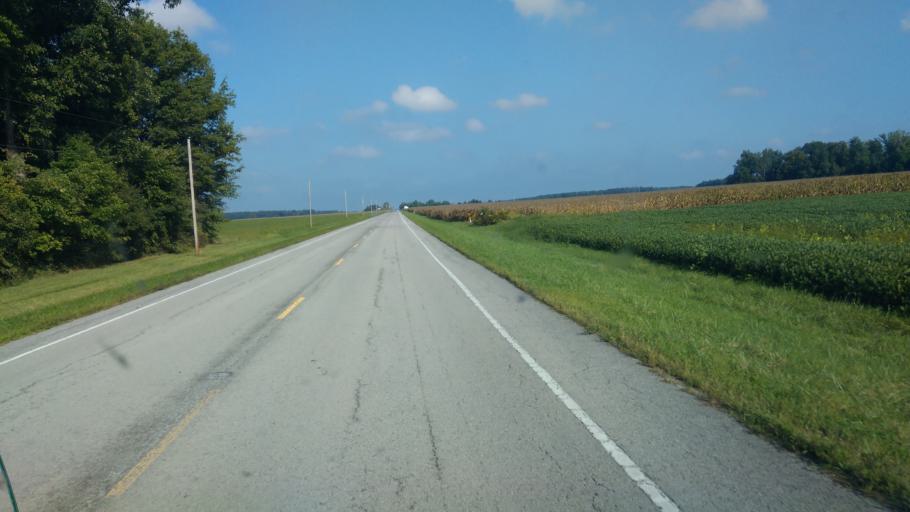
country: US
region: Ohio
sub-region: Hancock County
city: Arlington
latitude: 40.8338
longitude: -83.6246
